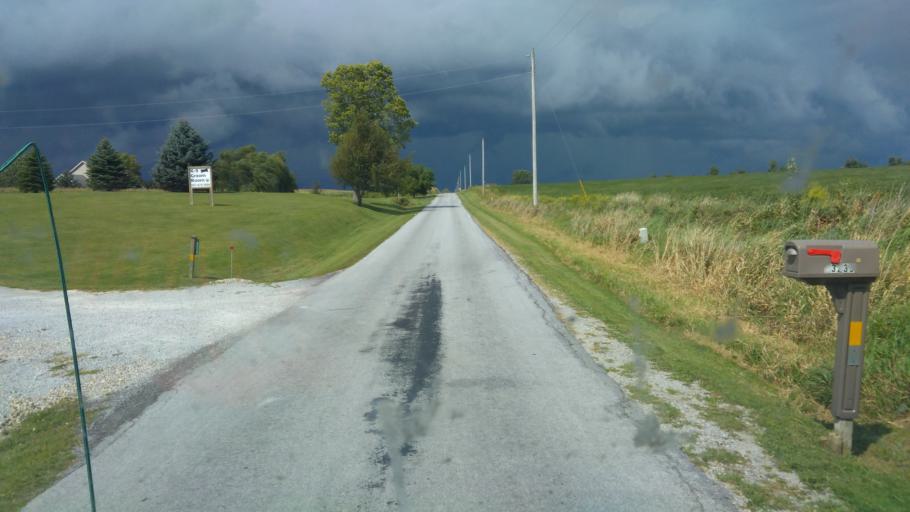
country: US
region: Ohio
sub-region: Hardin County
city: Kenton
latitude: 40.6252
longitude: -83.5159
